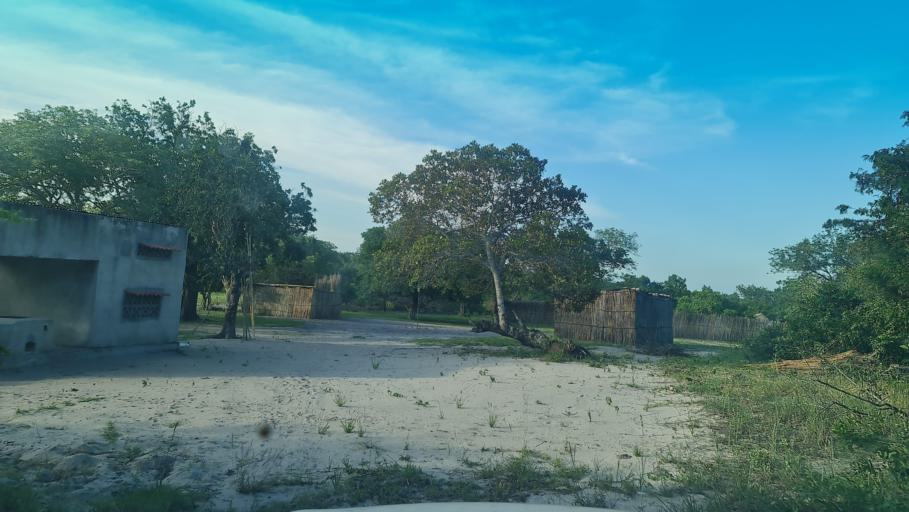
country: MZ
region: Gaza
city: Macia
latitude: -25.2287
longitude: 33.0158
